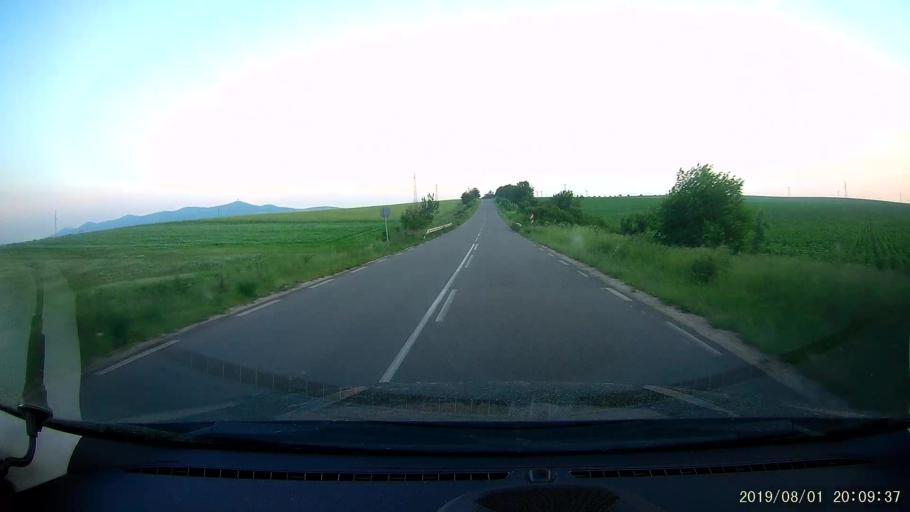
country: BG
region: Yambol
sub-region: Obshtina Yambol
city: Yambol
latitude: 42.4957
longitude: 26.5932
